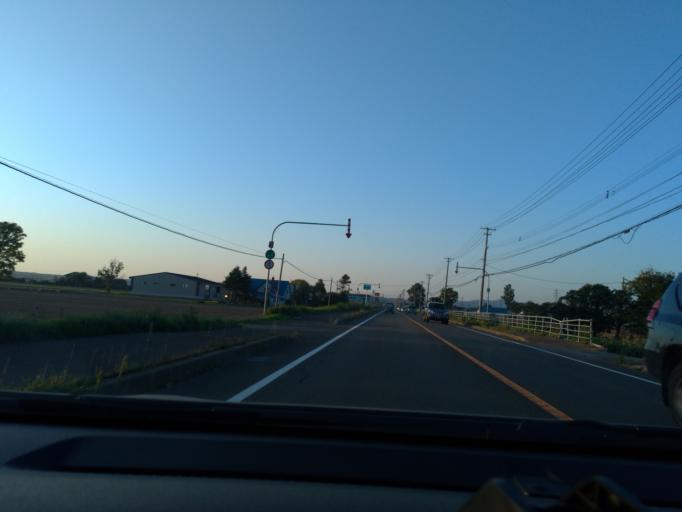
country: JP
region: Hokkaido
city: Tobetsu
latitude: 43.1971
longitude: 141.5228
